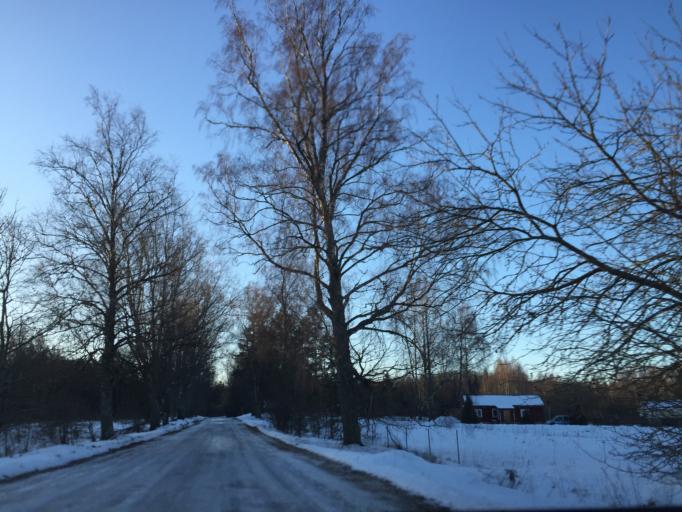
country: LV
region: Kegums
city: Kegums
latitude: 56.7421
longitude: 24.6664
